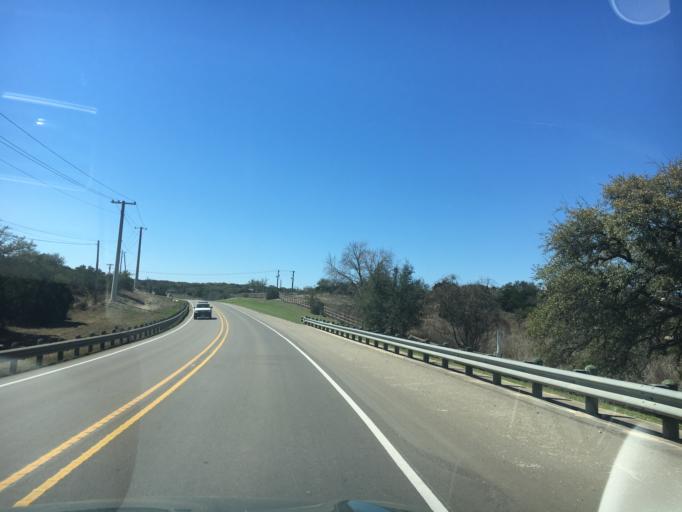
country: US
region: Texas
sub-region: Travis County
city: The Hills
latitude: 30.2915
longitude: -98.0413
